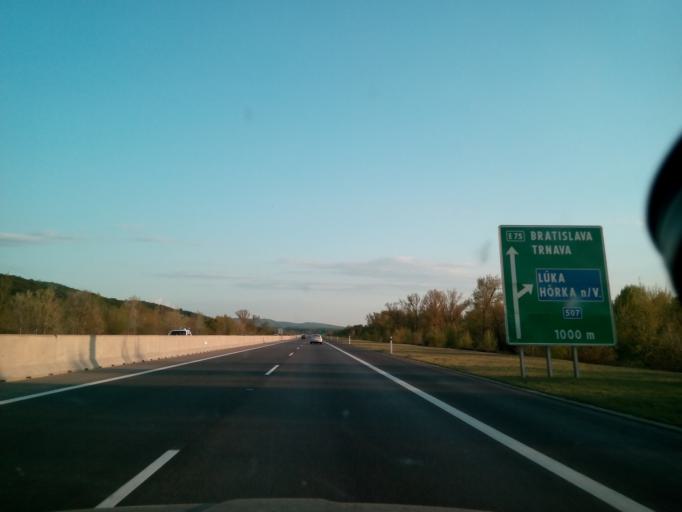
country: SK
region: Trenciansky
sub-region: Okres Nove Mesto nad Vahom
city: Nove Mesto nad Vahom
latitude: 48.6870
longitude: 17.8724
